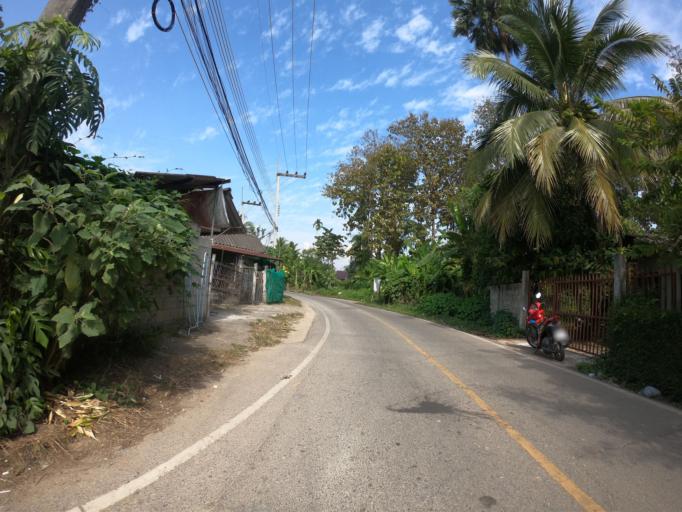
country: TH
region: Chiang Mai
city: San Sai
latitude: 18.8603
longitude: 99.0616
